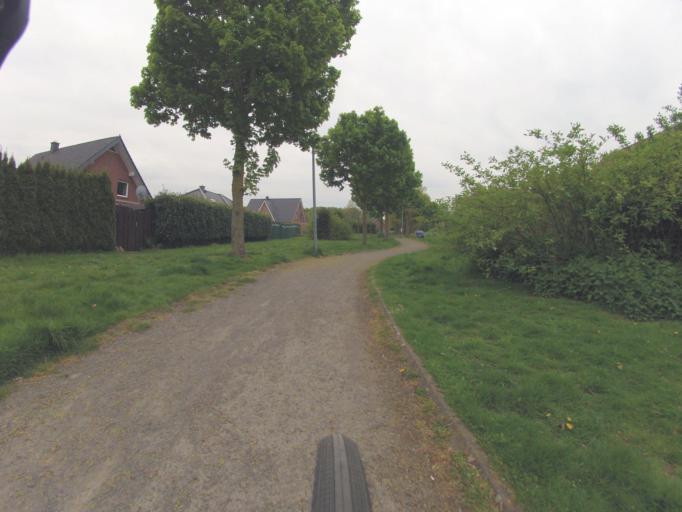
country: DE
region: North Rhine-Westphalia
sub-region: Regierungsbezirk Munster
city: Mettingen
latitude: 52.3100
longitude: 7.7895
